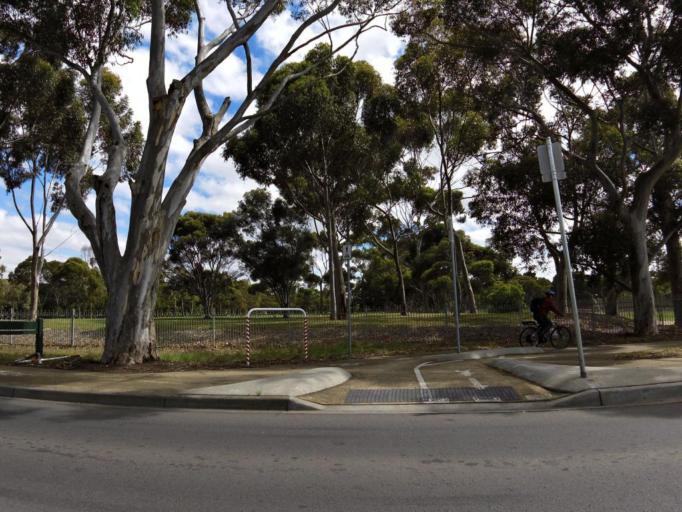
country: AU
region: Victoria
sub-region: Moreland
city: Fawkner
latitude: -37.7190
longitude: 144.9607
